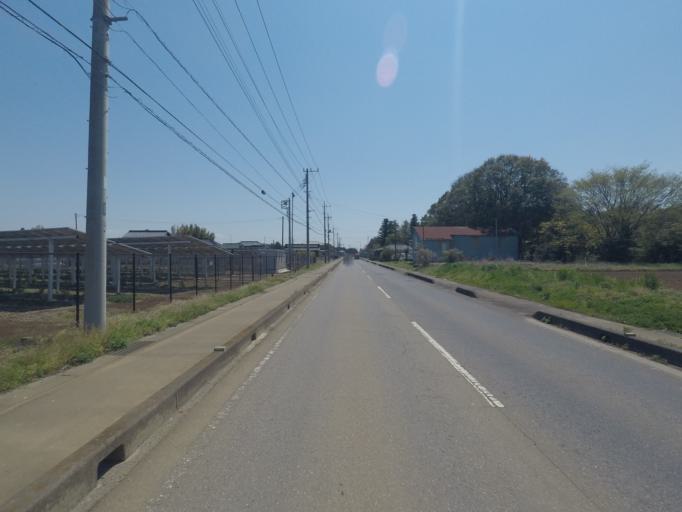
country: JP
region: Ibaraki
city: Ushiku
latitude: 35.9688
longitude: 140.0996
